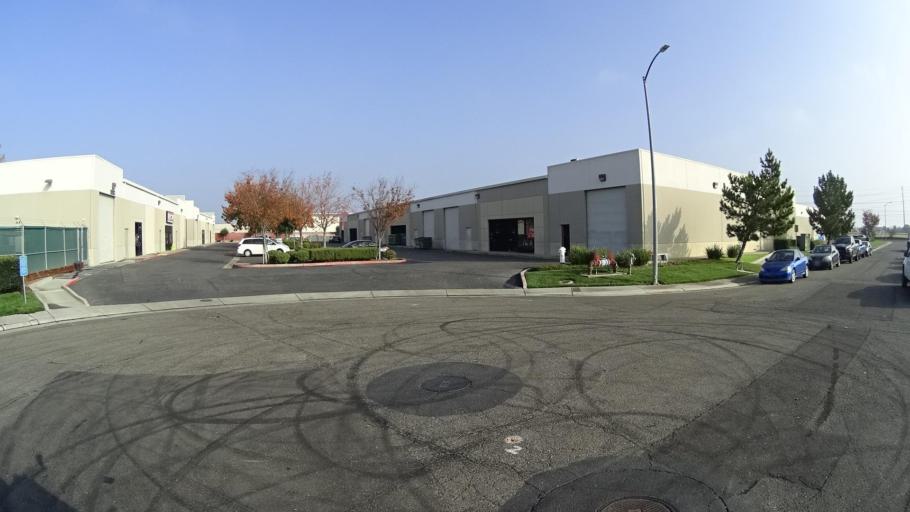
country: US
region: California
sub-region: Sacramento County
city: Elk Grove
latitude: 38.3996
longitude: -121.3546
